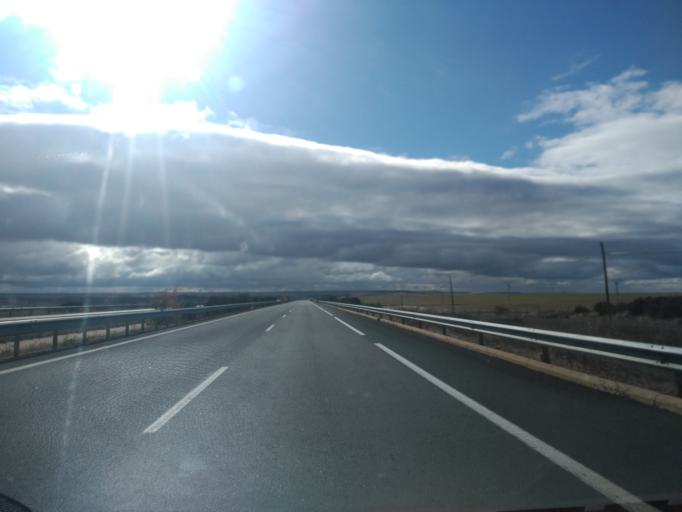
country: ES
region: Castille and Leon
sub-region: Provincia de Palencia
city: Fromista
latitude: 42.2909
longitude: -4.3999
